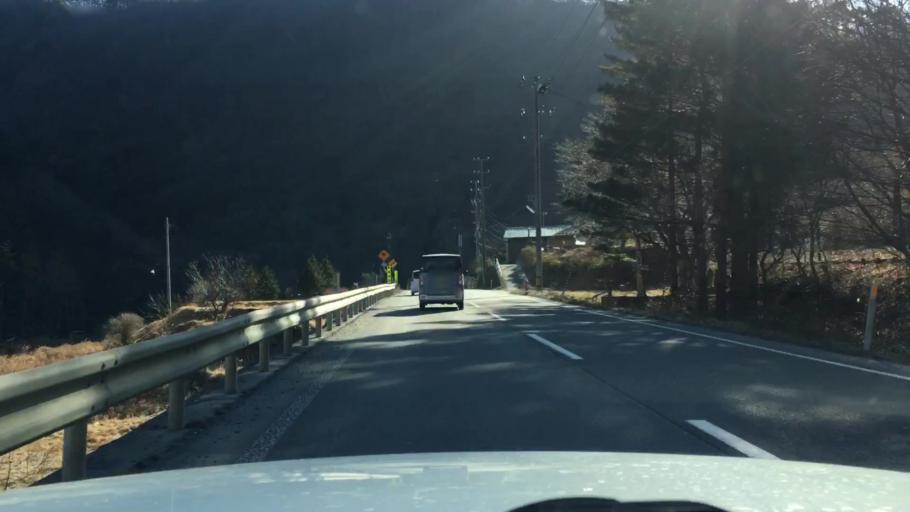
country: JP
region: Iwate
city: Miyako
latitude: 39.6081
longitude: 141.7870
